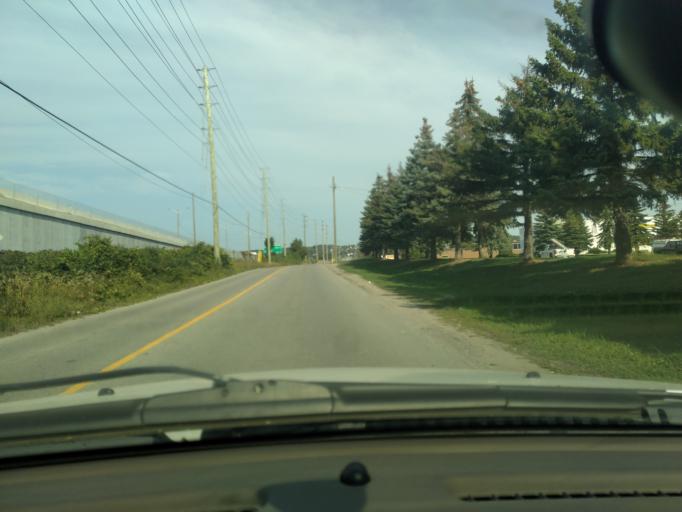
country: CA
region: Ontario
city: Barrie
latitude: 44.3719
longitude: -79.7078
